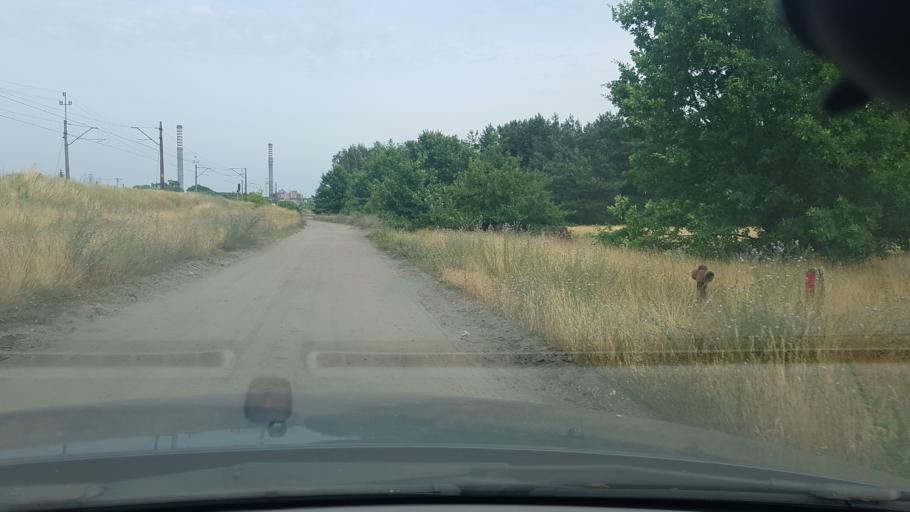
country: PL
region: Lodz Voivodeship
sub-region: Powiat tomaszowski
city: Tomaszow Mazowiecki
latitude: 51.5535
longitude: 20.0209
